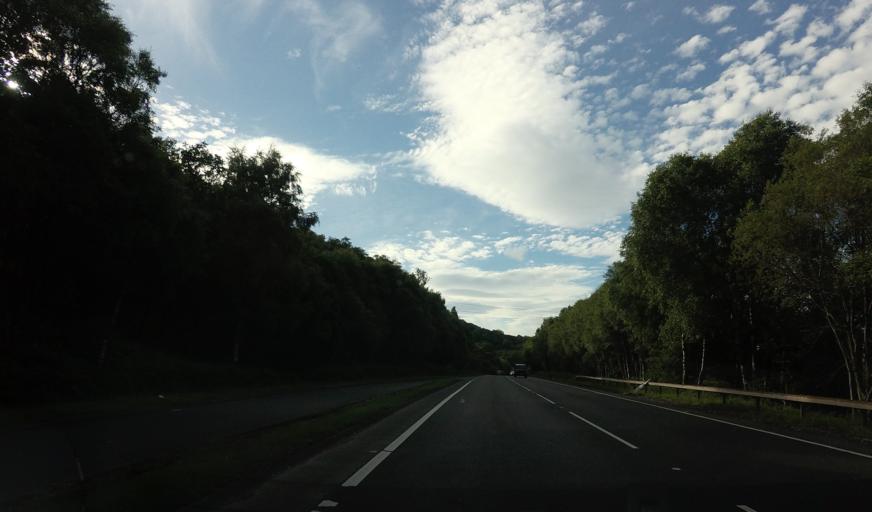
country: GB
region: Scotland
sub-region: Argyll and Bute
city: Helensburgh
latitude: 56.1720
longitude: -4.6815
